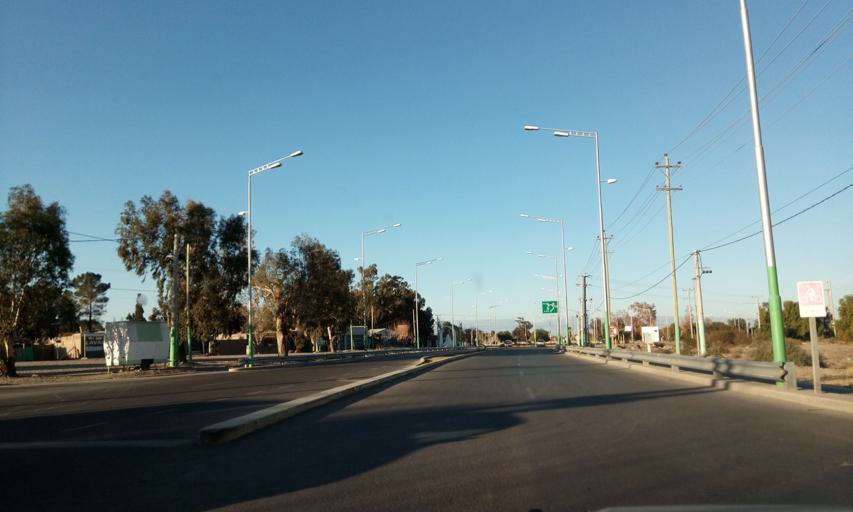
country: AR
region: San Juan
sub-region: Departamento de Rivadavia
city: Rivadavia
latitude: -31.5233
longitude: -68.6200
